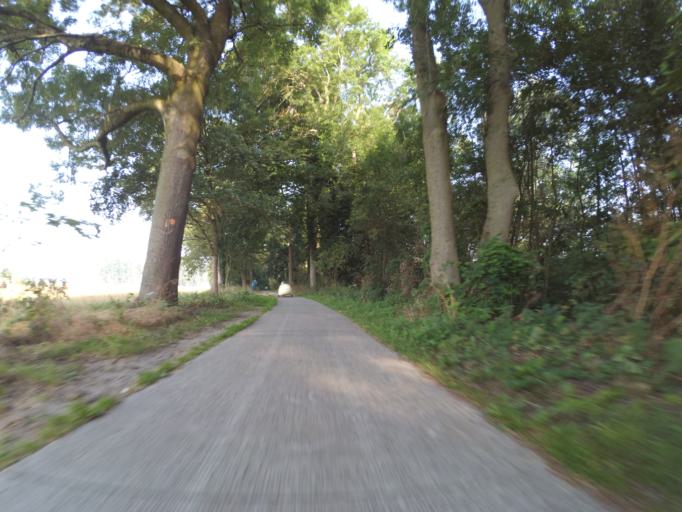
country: NL
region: Overijssel
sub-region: Gemeente Wierden
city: Wierden
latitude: 52.3194
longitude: 6.5636
